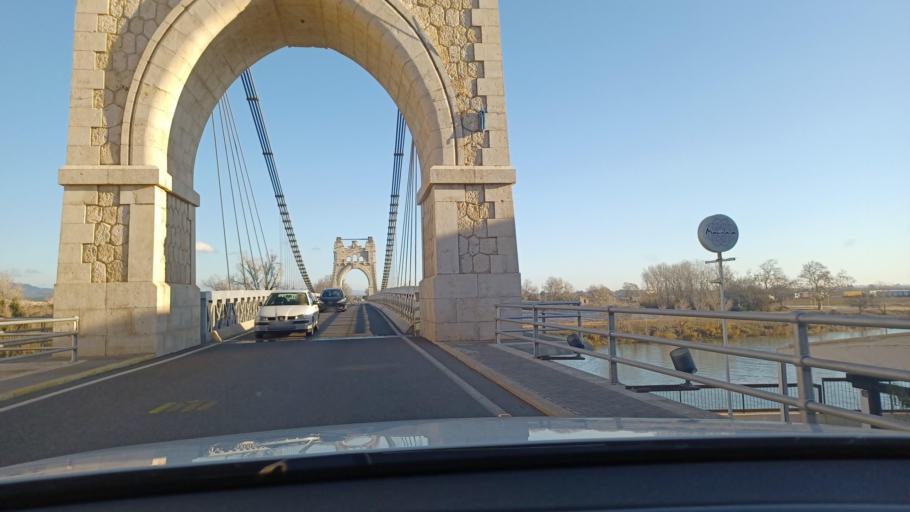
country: ES
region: Catalonia
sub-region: Provincia de Tarragona
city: Amposta
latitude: 40.7142
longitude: 0.5813
